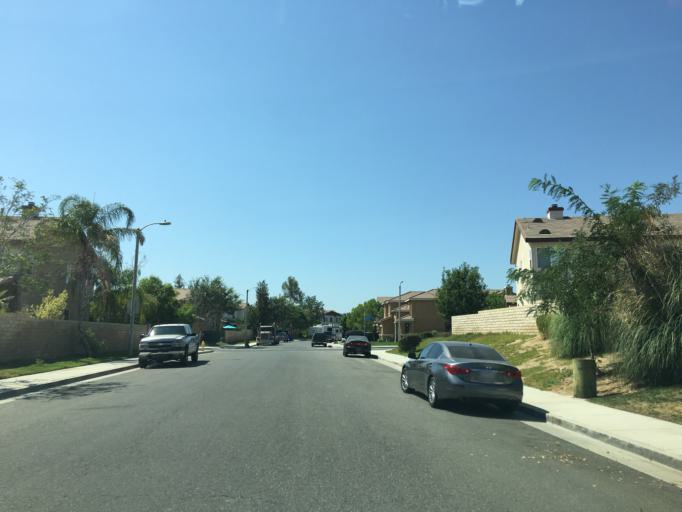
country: US
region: California
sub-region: Los Angeles County
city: Val Verde
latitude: 34.4703
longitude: -118.6456
